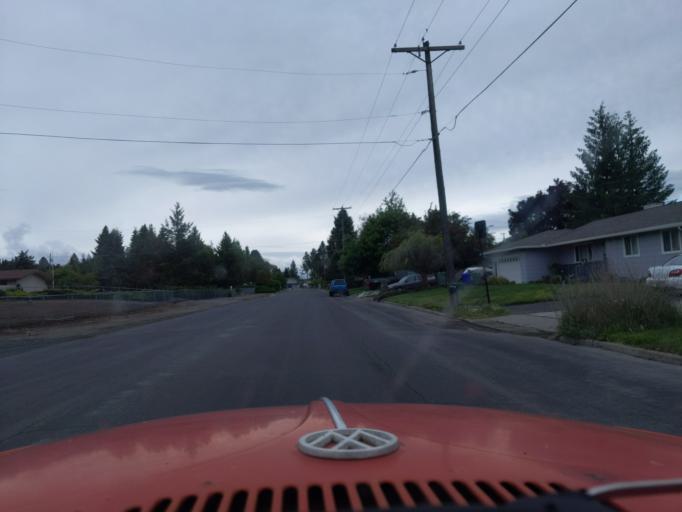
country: US
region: Washington
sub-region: Spokane County
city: Spokane
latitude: 47.5999
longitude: -117.3792
